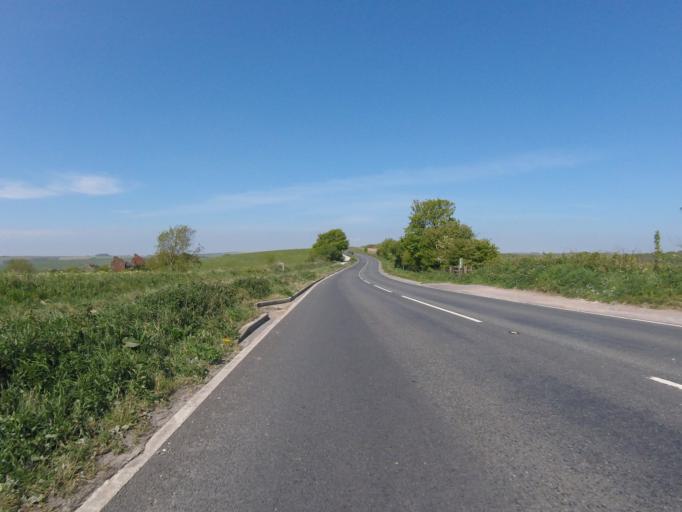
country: GB
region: England
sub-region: Brighton and Hove
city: Brighton
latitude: 50.8622
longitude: -0.1210
